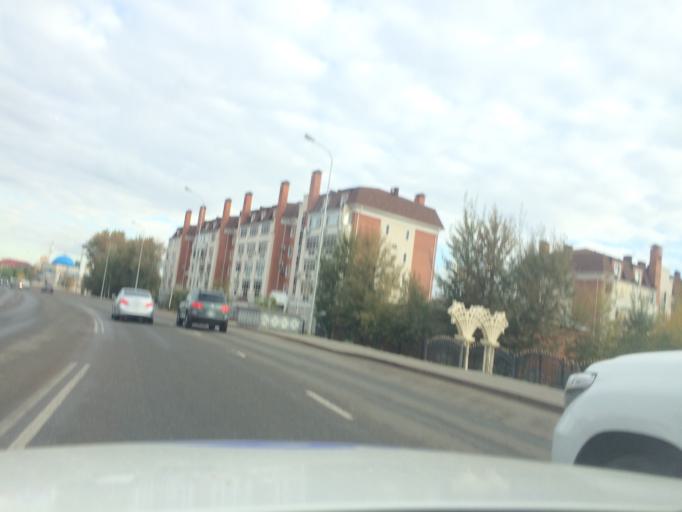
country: KZ
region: Astana Qalasy
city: Astana
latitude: 51.1361
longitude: 71.4356
